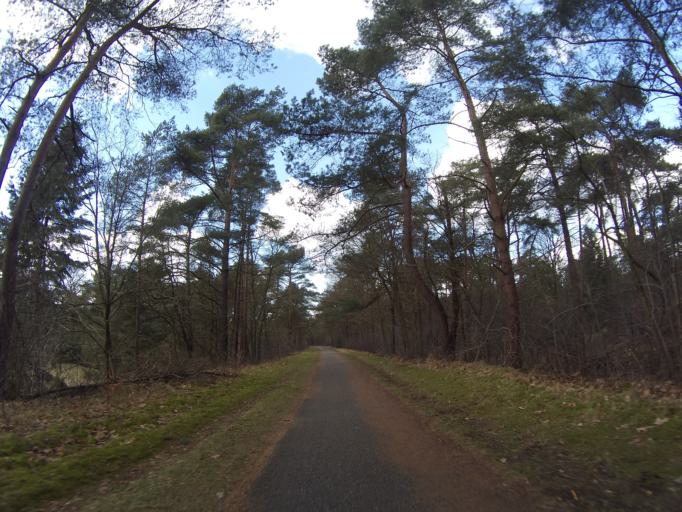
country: NL
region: Utrecht
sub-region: Gemeente Zeist
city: Zeist
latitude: 52.1215
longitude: 5.2350
